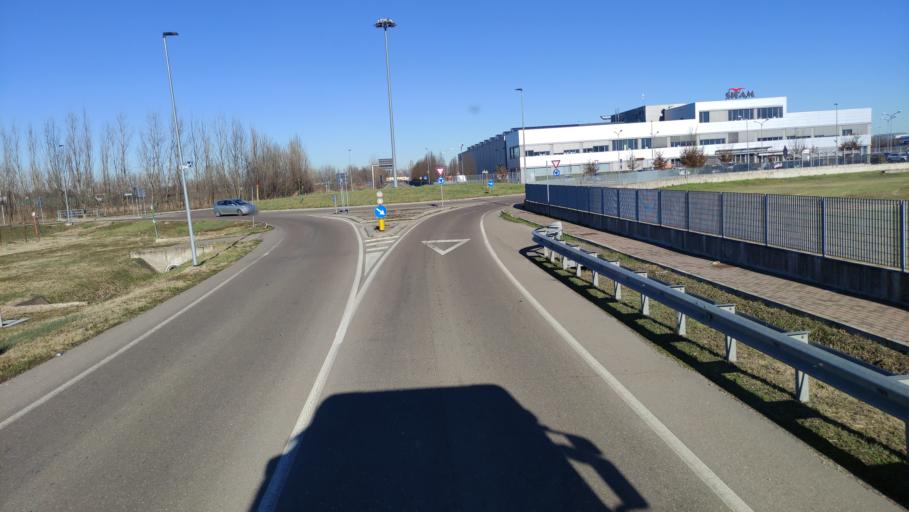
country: IT
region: Emilia-Romagna
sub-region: Provincia di Reggio Emilia
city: Correggio
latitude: 44.7713
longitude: 10.8132
